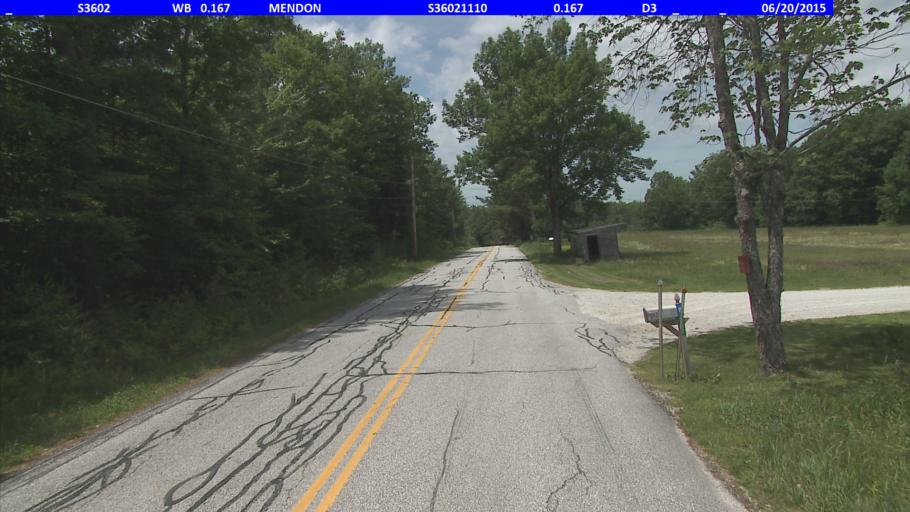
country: US
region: Vermont
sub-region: Rutland County
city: Rutland
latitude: 43.6460
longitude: -72.9350
